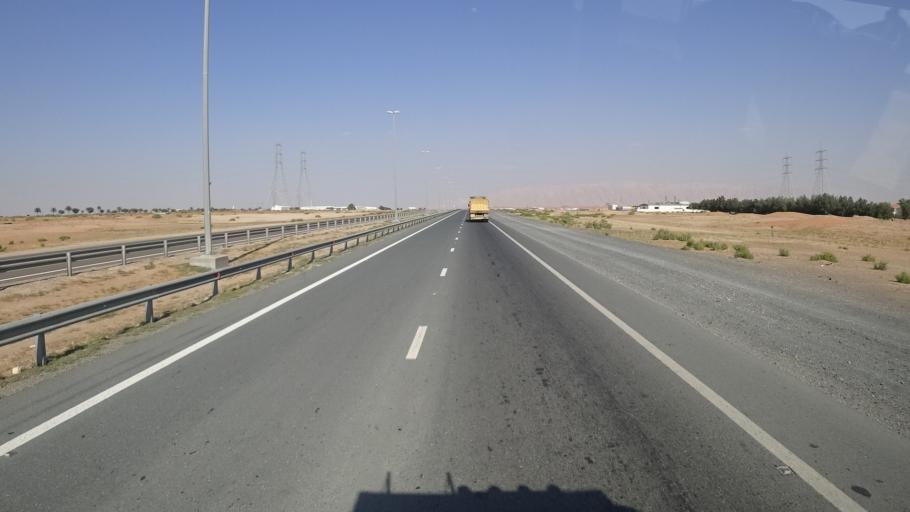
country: AE
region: Abu Dhabi
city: Al Ain
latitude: 24.0497
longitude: 55.6107
